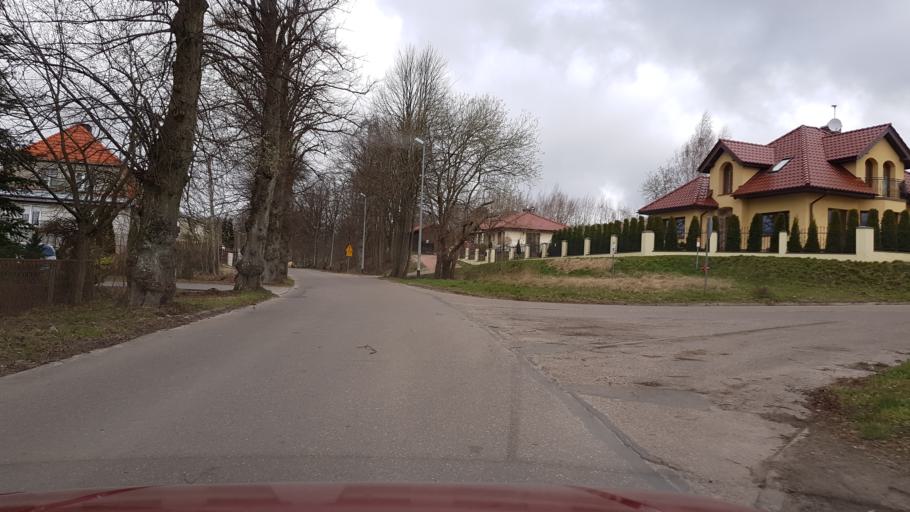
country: PL
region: West Pomeranian Voivodeship
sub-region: Powiat koszalinski
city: Sianow
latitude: 54.1817
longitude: 16.2453
